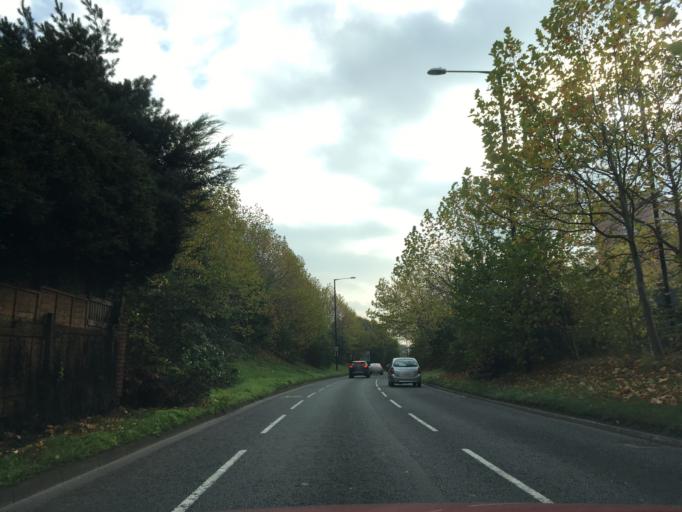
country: GB
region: England
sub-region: Bristol
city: Bristol
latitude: 51.4653
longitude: -2.5734
